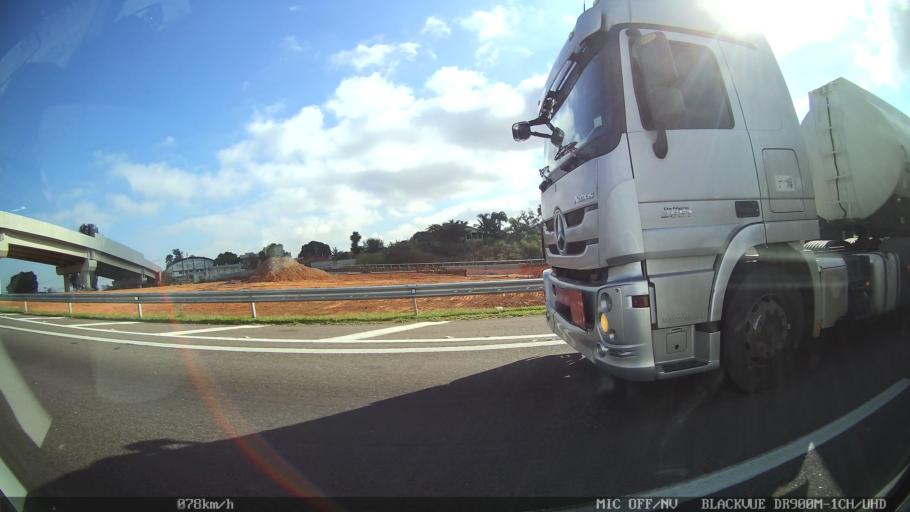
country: BR
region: Sao Paulo
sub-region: Hortolandia
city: Hortolandia
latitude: -22.8852
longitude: -47.1566
